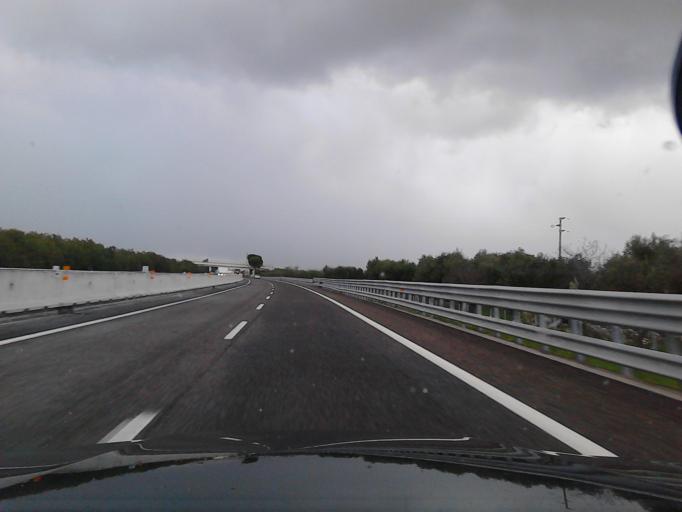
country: IT
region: Apulia
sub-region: Provincia di Bari
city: Bitonto
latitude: 41.1341
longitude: 16.7094
